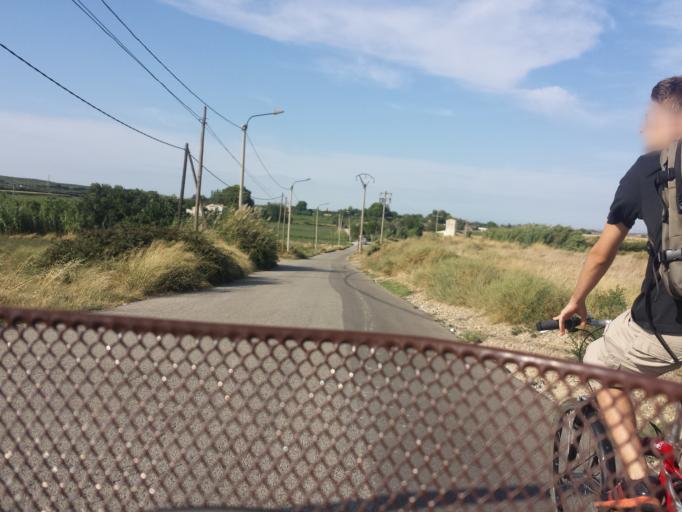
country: ES
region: Aragon
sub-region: Provincia de Zaragoza
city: Zaragoza
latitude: 41.6938
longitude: -0.8619
